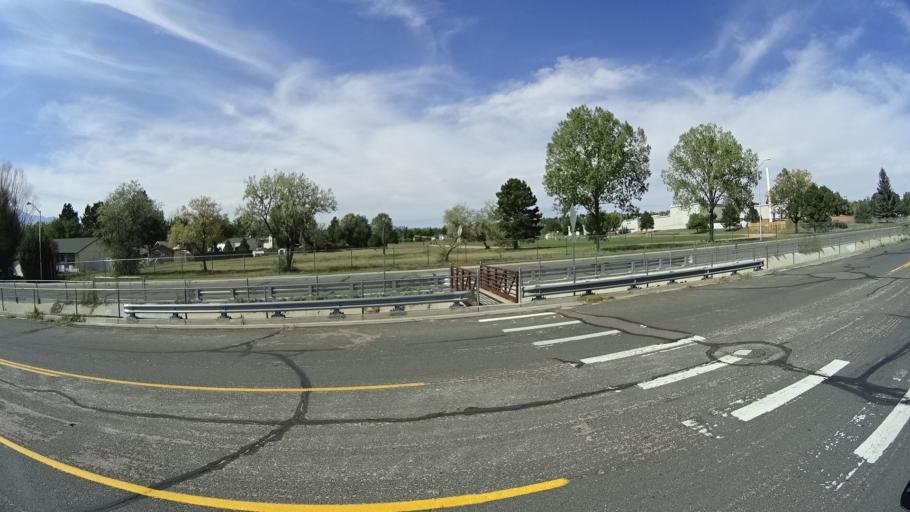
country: US
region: Colorado
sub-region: El Paso County
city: Cimarron Hills
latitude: 38.9019
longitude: -104.7566
